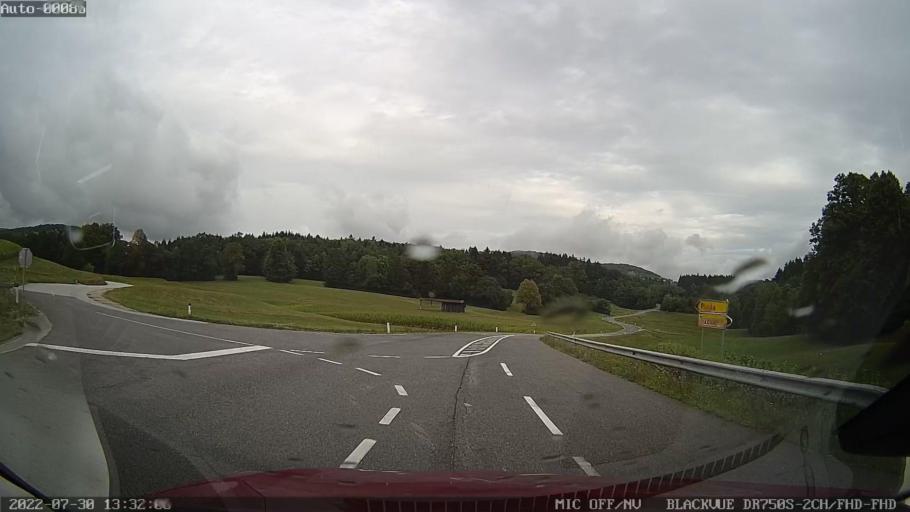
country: SI
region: Zuzemberk
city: Zuzemberk
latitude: 45.8405
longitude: 14.9388
